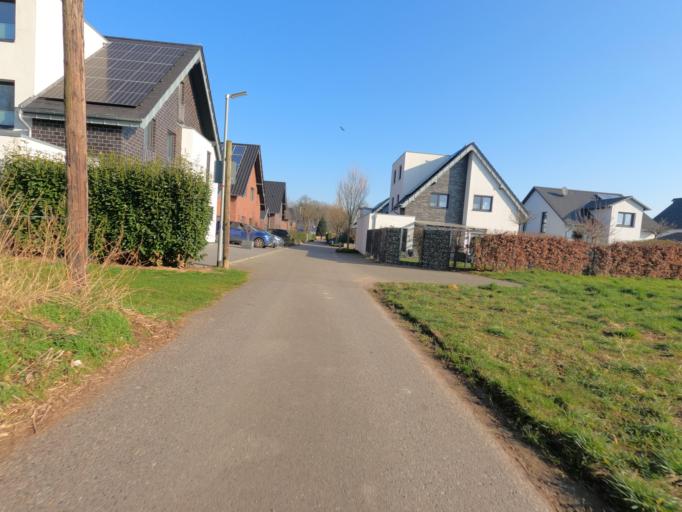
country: DE
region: North Rhine-Westphalia
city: Erkelenz
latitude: 51.0790
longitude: 6.2864
